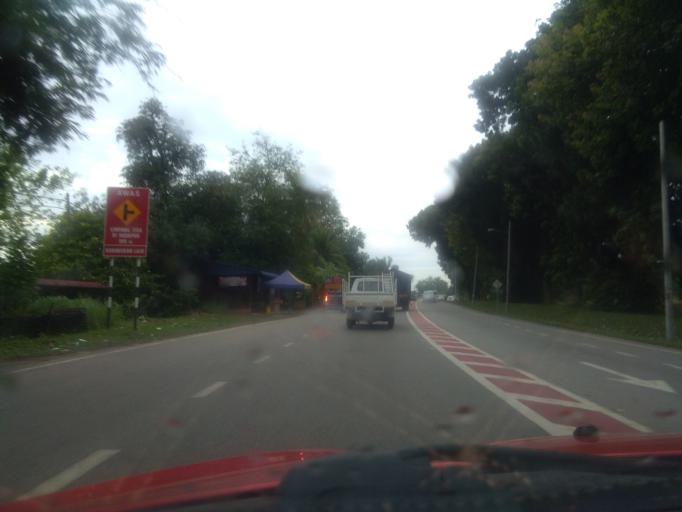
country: MY
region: Kedah
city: Sungai Petani
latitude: 5.6299
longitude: 100.5241
